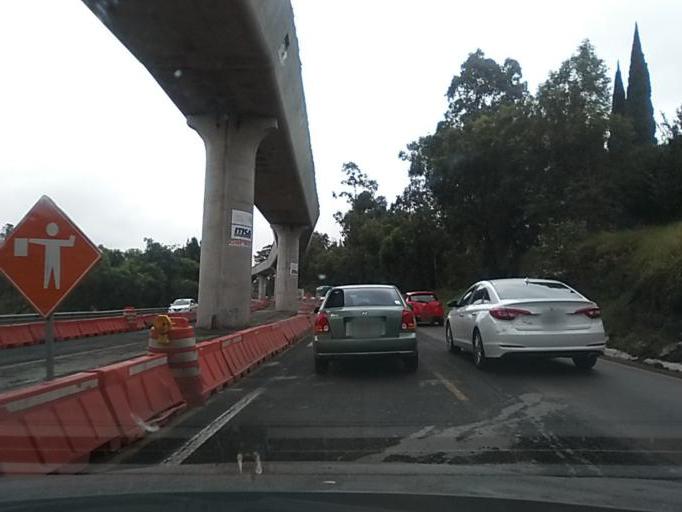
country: MX
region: Mexico City
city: Xochimilco
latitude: 19.2470
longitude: -99.1537
